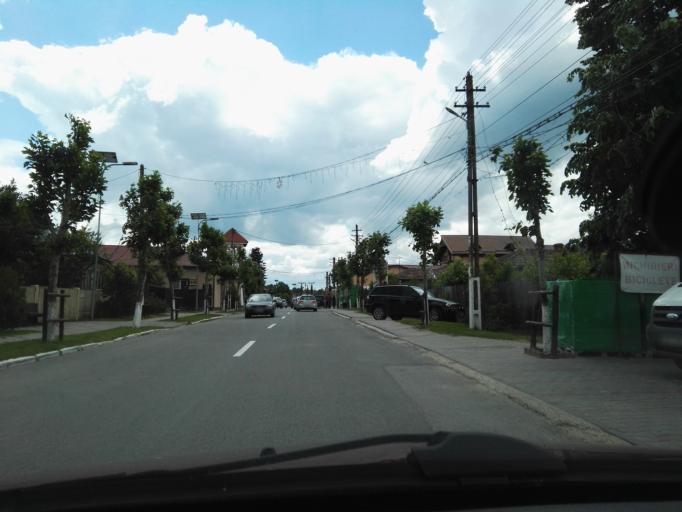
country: RO
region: Giurgiu
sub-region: Comuna Comana
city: Comana
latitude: 44.1735
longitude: 26.1448
